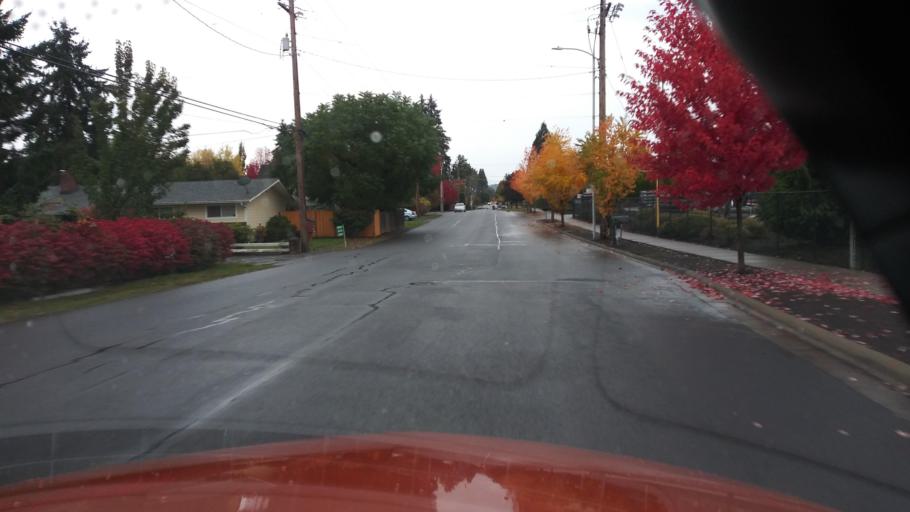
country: US
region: Oregon
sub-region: Washington County
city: Forest Grove
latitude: 45.5262
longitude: -123.0991
